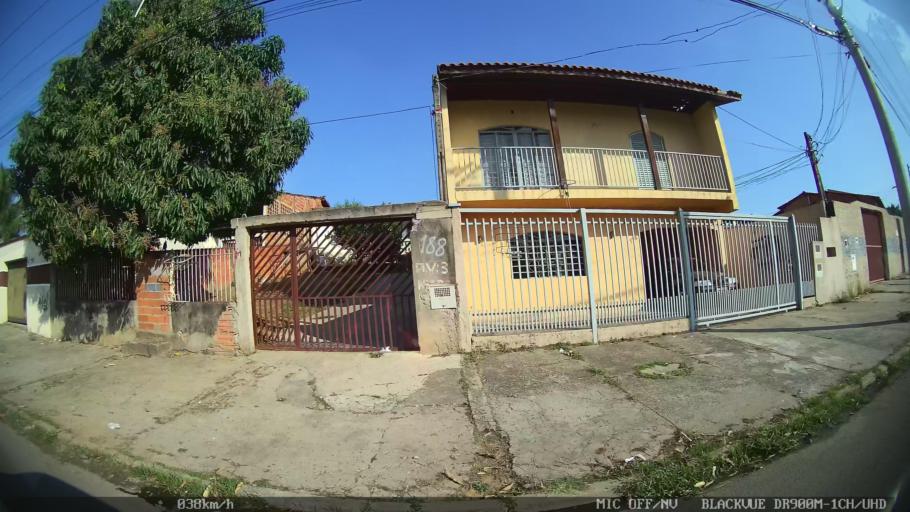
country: BR
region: Sao Paulo
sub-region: Campinas
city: Campinas
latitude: -22.9848
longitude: -47.1355
